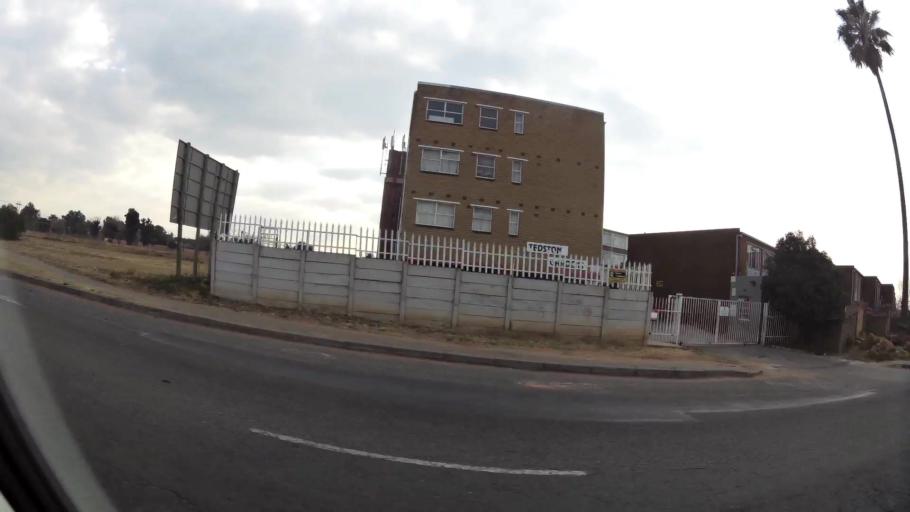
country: ZA
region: Gauteng
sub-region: Ekurhuleni Metropolitan Municipality
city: Germiston
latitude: -26.2386
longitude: 28.1956
